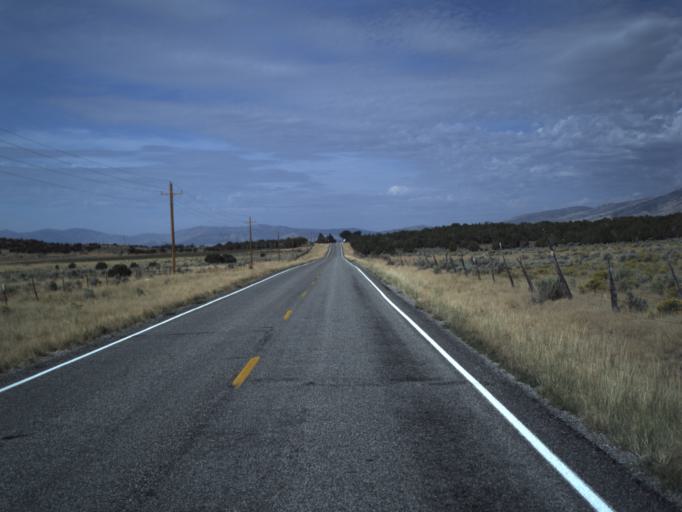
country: US
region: Idaho
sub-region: Cassia County
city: Burley
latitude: 41.8172
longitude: -113.2934
